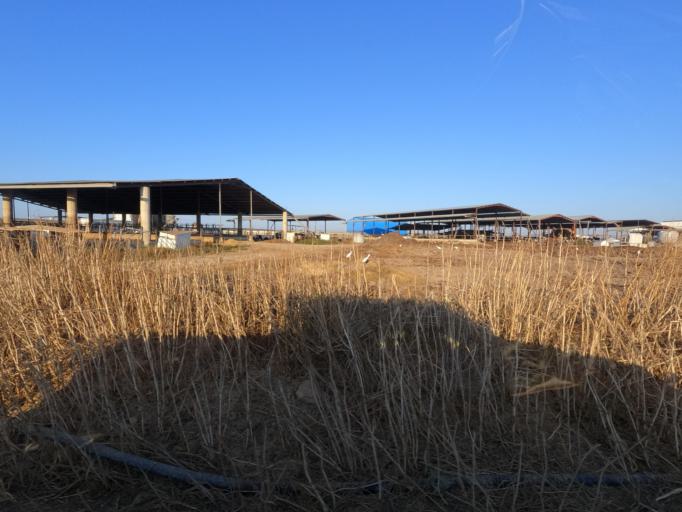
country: CY
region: Ammochostos
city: Achna
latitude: 35.0354
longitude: 33.7885
